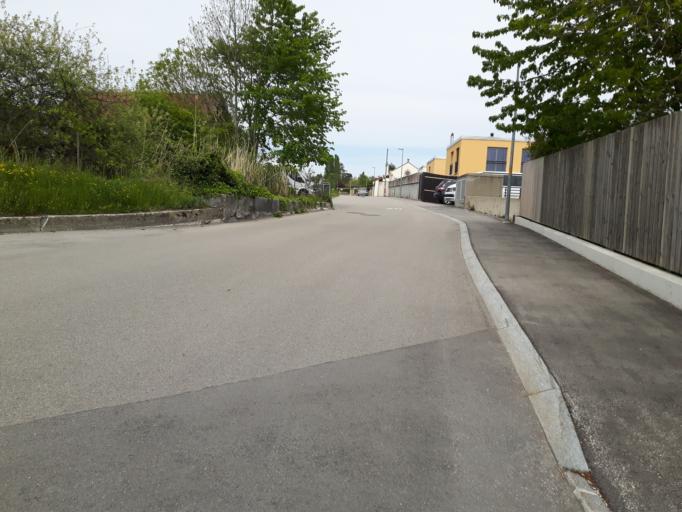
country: CH
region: Neuchatel
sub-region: Boudry District
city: Bevaix
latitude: 46.9233
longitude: 6.8170
